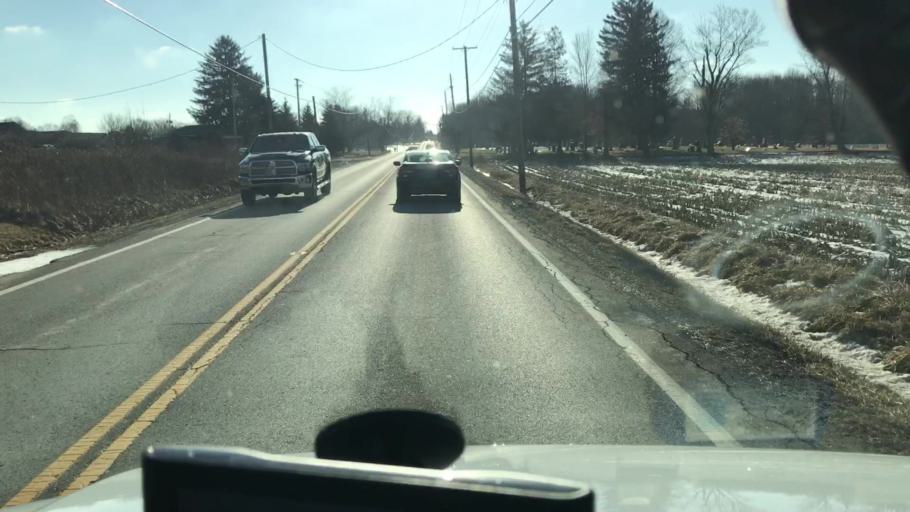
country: US
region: Ohio
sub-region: Mahoning County
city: New Middletown
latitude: 40.9280
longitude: -80.6224
